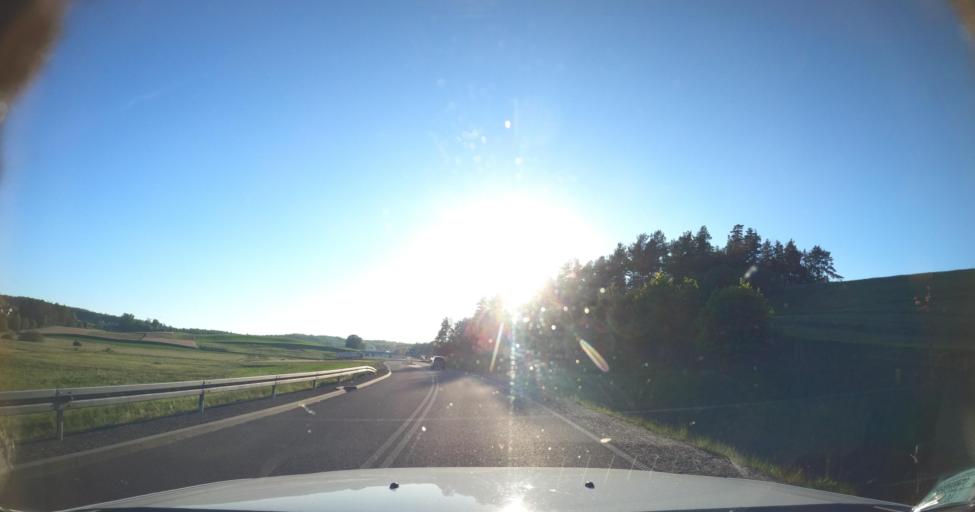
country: PL
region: Pomeranian Voivodeship
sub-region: Powiat kartuski
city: Chmielno
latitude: 54.3427
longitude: 18.0123
